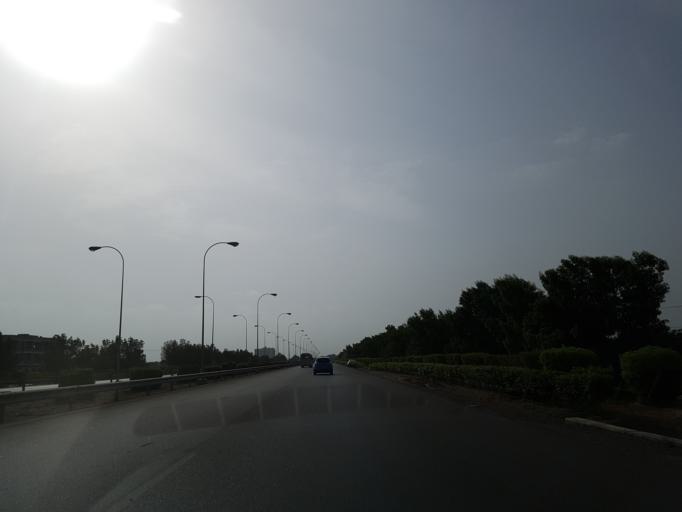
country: OM
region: Al Batinah
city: Al Sohar
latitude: 24.4018
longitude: 56.6610
